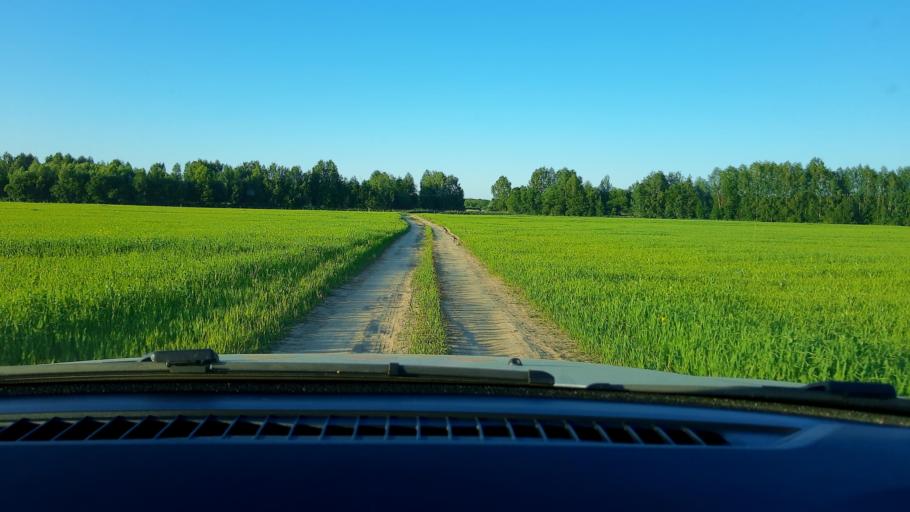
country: RU
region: Nizjnij Novgorod
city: Kstovo
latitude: 56.3050
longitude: 44.2619
